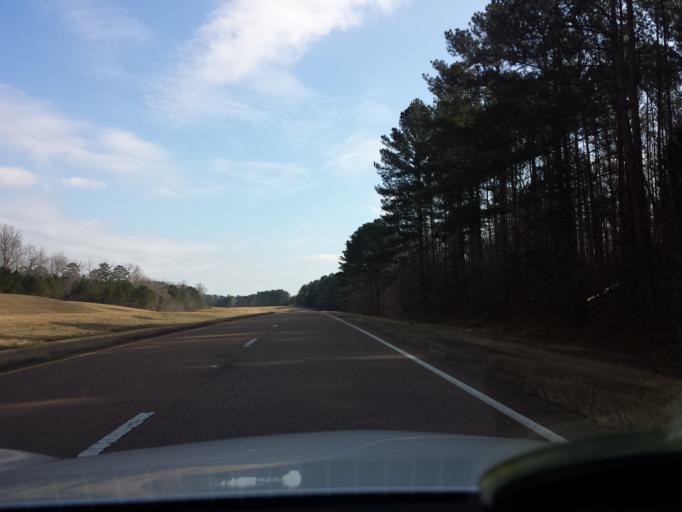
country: US
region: Mississippi
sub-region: Winston County
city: Louisville
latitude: 33.1710
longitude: -89.0514
